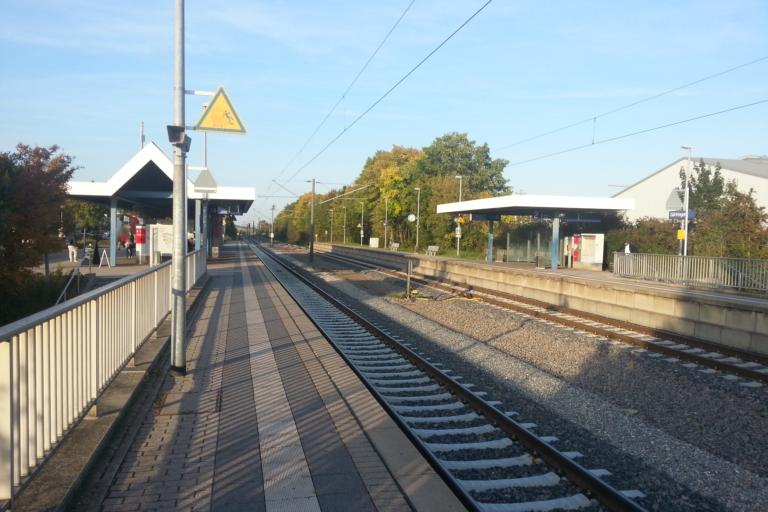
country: DE
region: Baden-Wuerttemberg
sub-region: Regierungsbezirk Stuttgart
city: Gartringen
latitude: 48.6405
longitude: 8.9088
